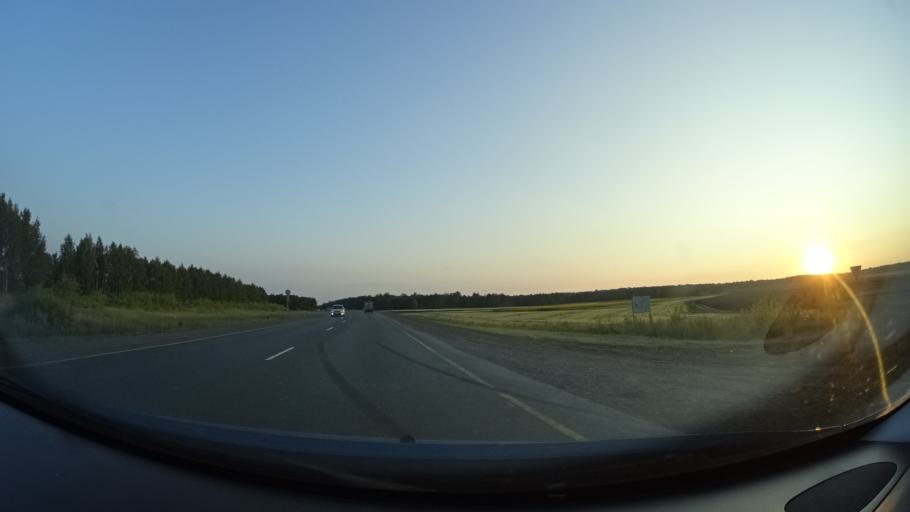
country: RU
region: Samara
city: Sernovodsk
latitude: 53.9271
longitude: 51.3205
